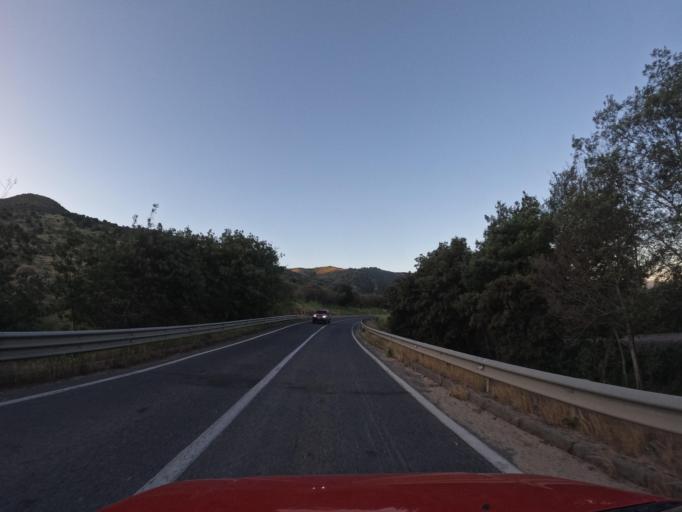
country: CL
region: Maule
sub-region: Provincia de Curico
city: Rauco
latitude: -35.0752
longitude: -71.6273
